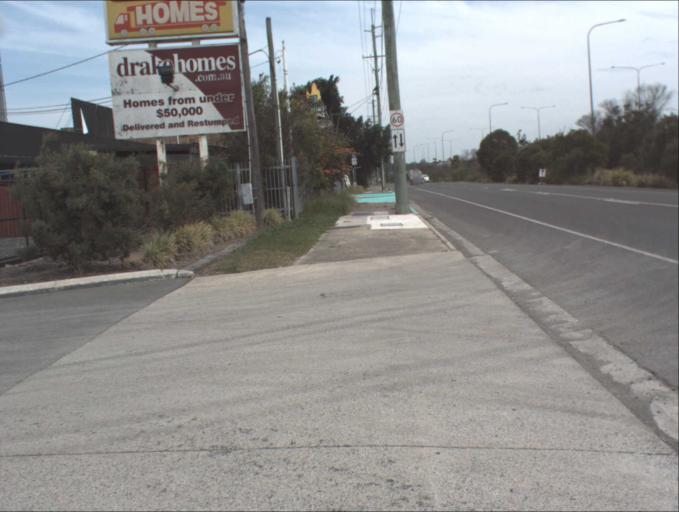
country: AU
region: Queensland
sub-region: Logan
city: Beenleigh
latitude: -27.6887
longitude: 153.1917
